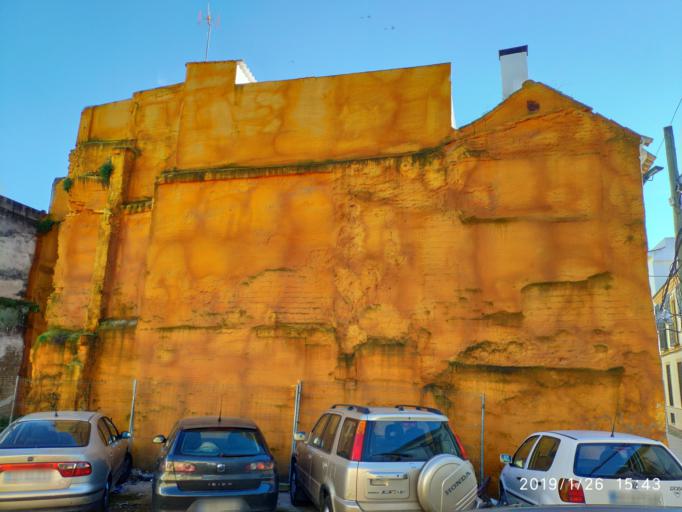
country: ES
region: Andalusia
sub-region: Province of Cordoba
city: Cordoba
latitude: 37.8848
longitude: -4.7740
